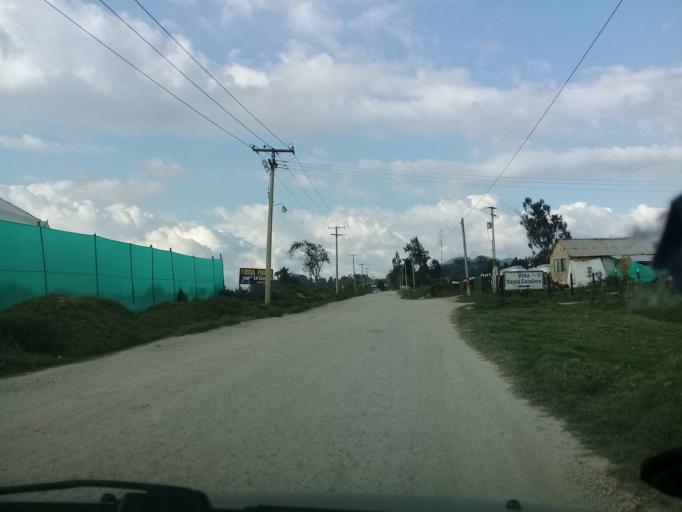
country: CO
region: Cundinamarca
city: Madrid
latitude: 4.7827
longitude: -74.2207
